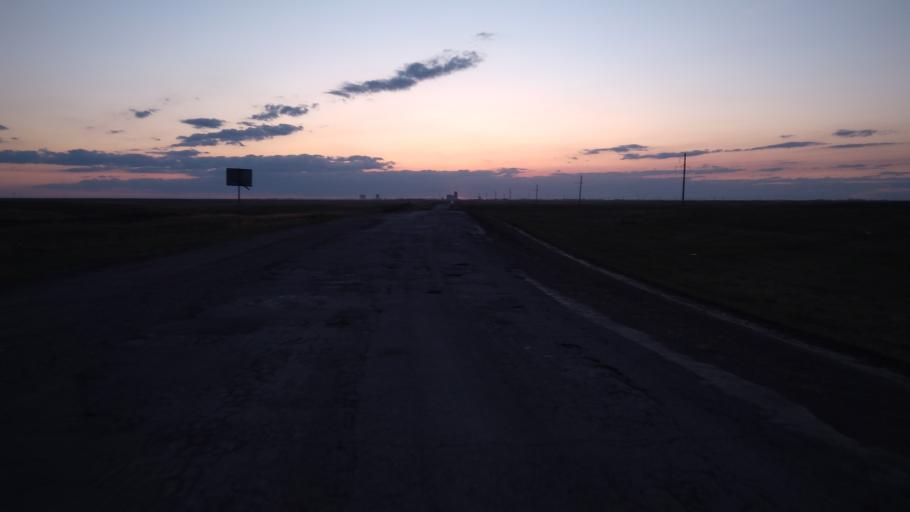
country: RU
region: Chelyabinsk
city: Troitsk
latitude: 54.0873
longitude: 61.6571
